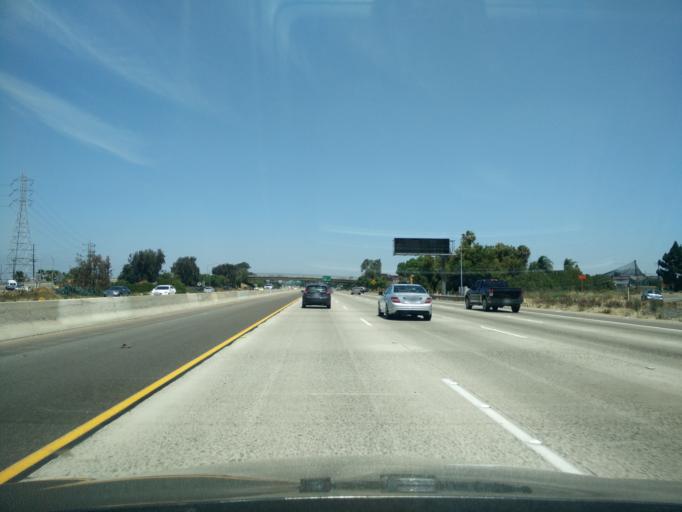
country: US
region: California
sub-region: San Diego County
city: Chula Vista
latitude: 32.6119
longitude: -117.0908
